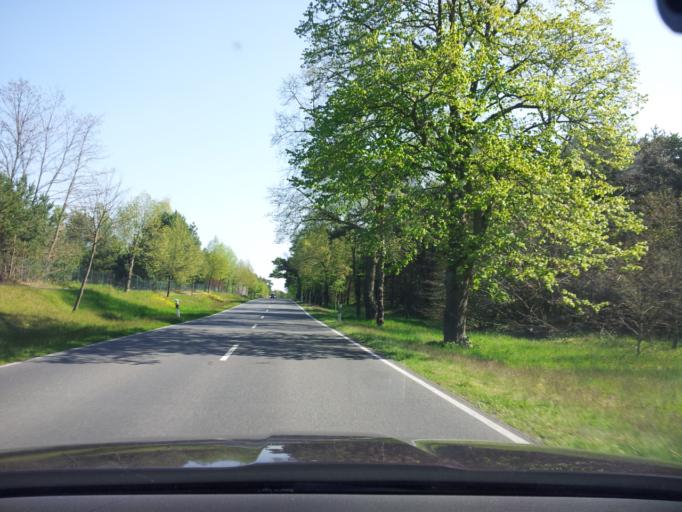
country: DE
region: Brandenburg
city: Juterbog
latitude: 52.0065
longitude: 13.0623
